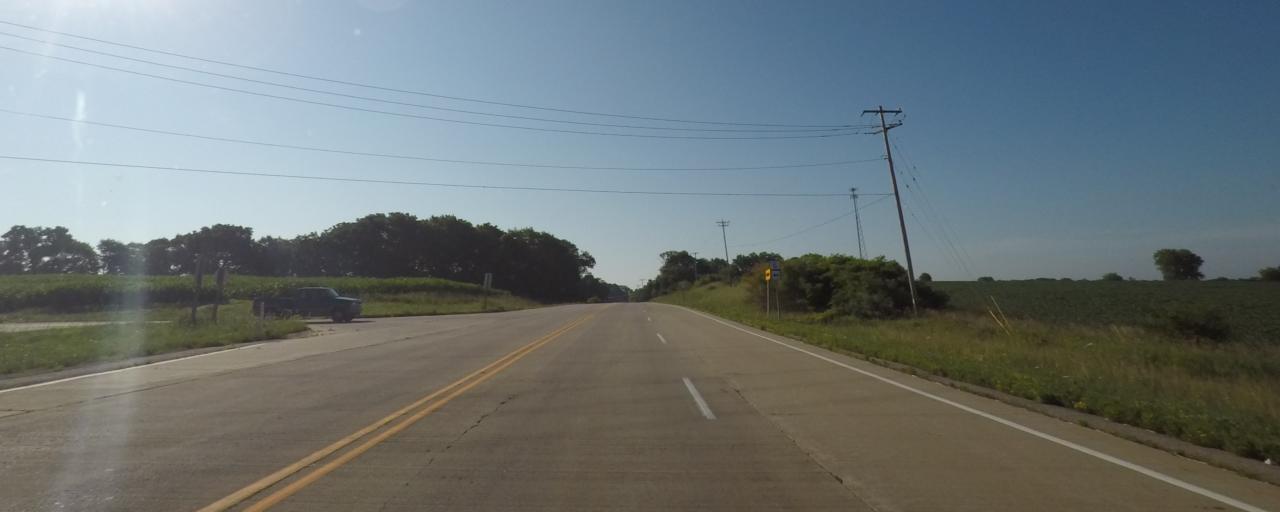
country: US
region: Wisconsin
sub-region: Jefferson County
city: Lake Koshkonong
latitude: 42.9594
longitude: -88.8919
